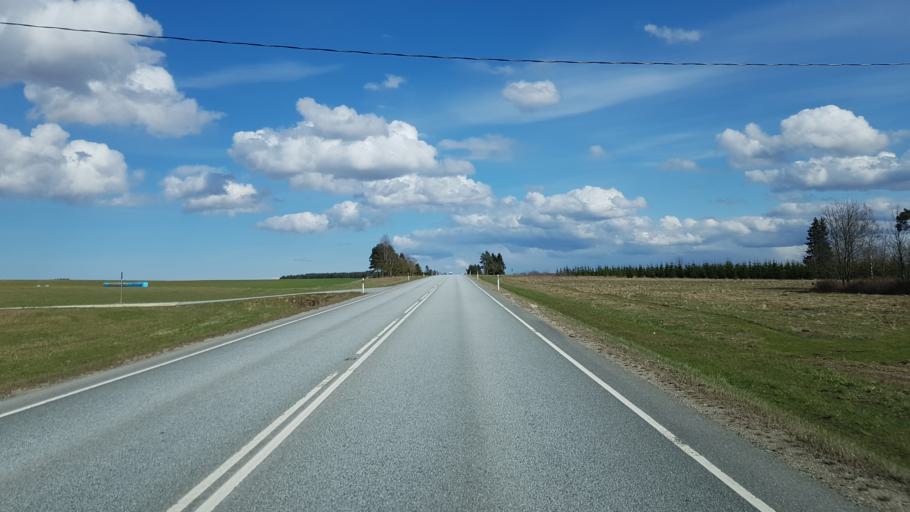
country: EE
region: Laeaene-Virumaa
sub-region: Haljala vald
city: Haljala
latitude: 59.4205
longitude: 26.2955
